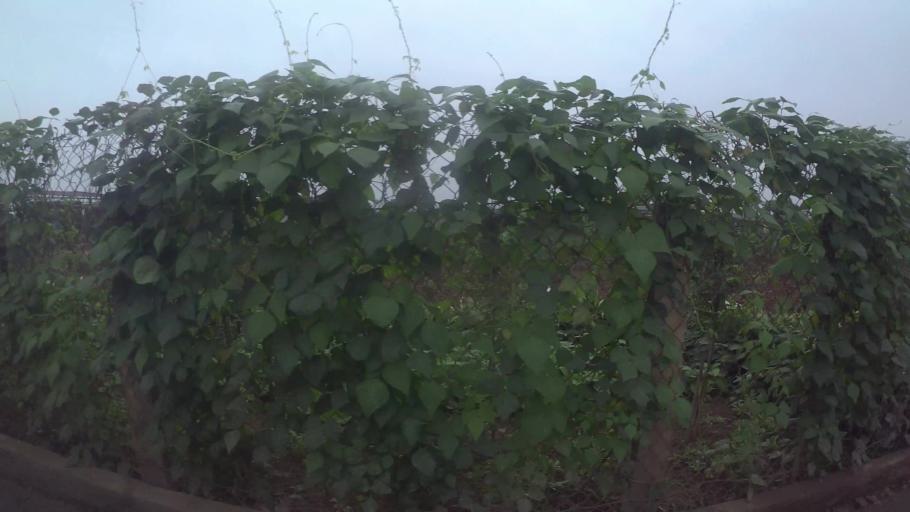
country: VN
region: Ha Noi
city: Tay Ho
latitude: 21.0749
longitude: 105.8266
